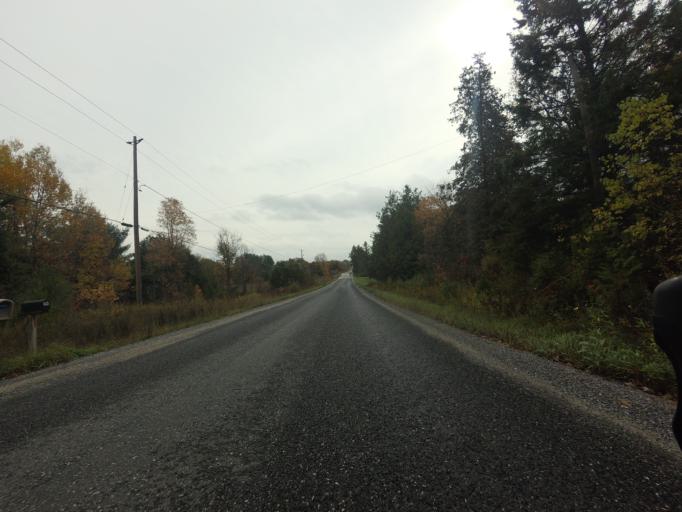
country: CA
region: Ontario
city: Perth
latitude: 45.1234
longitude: -76.5224
